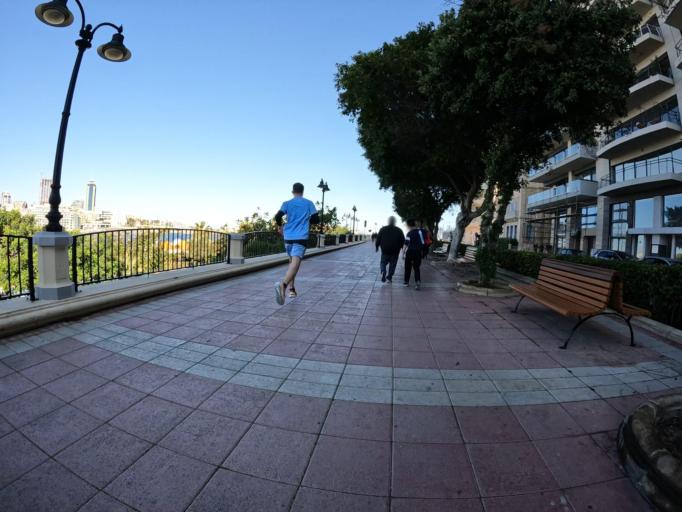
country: MT
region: Tas-Sliema
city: Sliema
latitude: 35.9167
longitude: 14.4985
